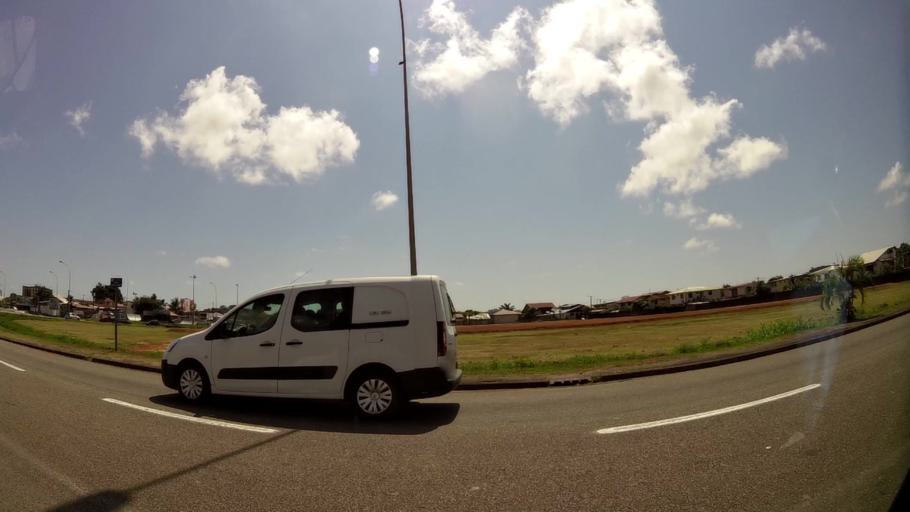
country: GF
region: Guyane
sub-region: Guyane
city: Cayenne
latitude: 4.9314
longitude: -52.3265
